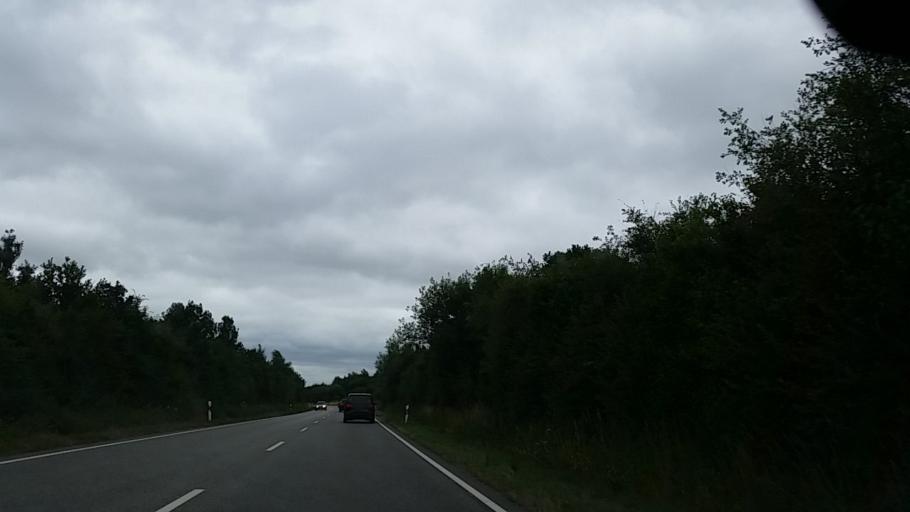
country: DE
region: Schleswig-Holstein
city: Tuttendorf
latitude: 54.4044
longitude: 10.0032
